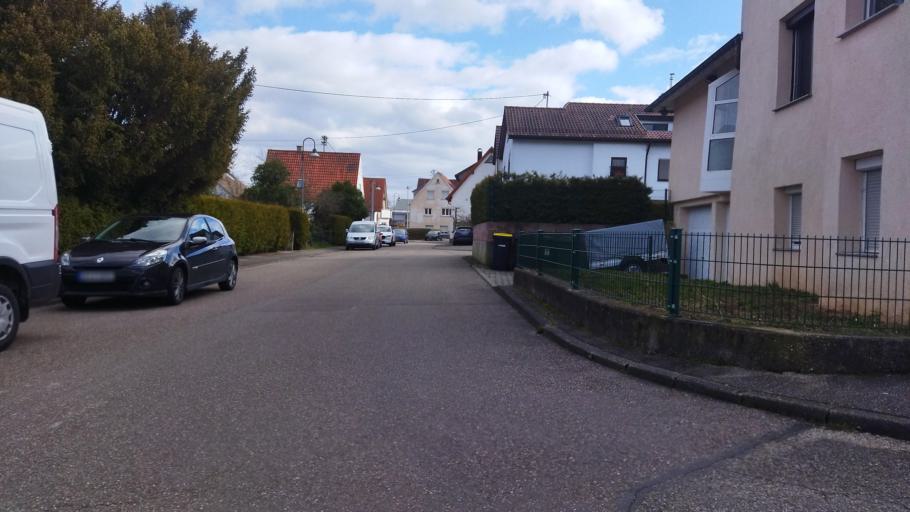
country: DE
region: Baden-Wuerttemberg
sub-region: Regierungsbezirk Stuttgart
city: Freudental
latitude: 49.0111
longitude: 9.0572
